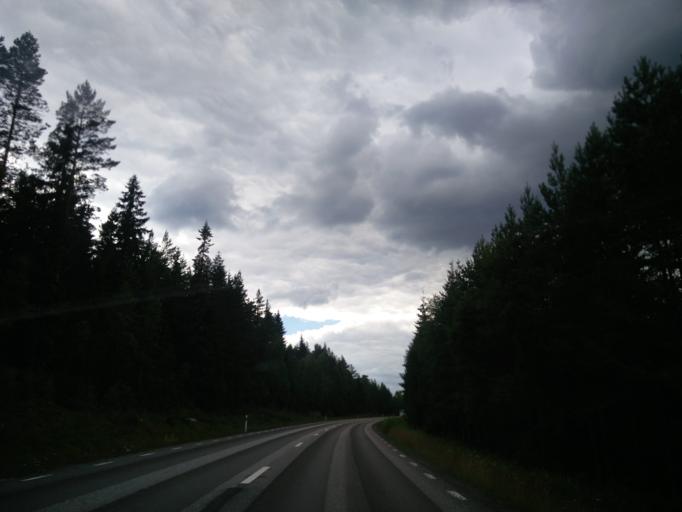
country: SE
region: OErebro
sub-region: Hallefors Kommun
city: Haellefors
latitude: 59.7855
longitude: 14.3579
